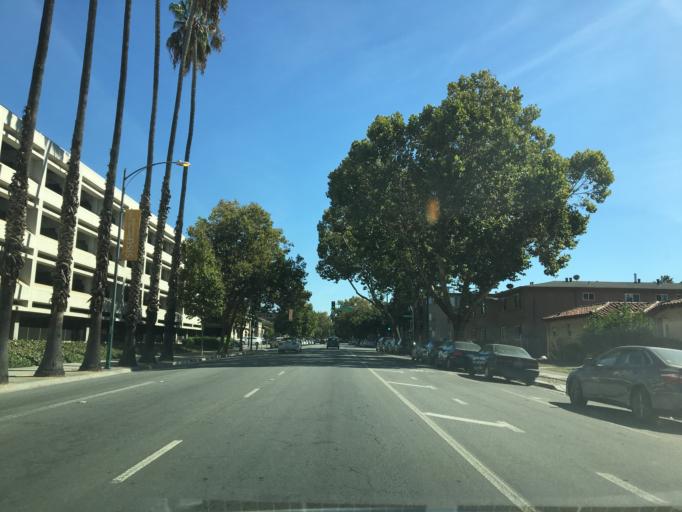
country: US
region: California
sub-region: Santa Clara County
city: San Jose
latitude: 37.3323
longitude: -121.8834
